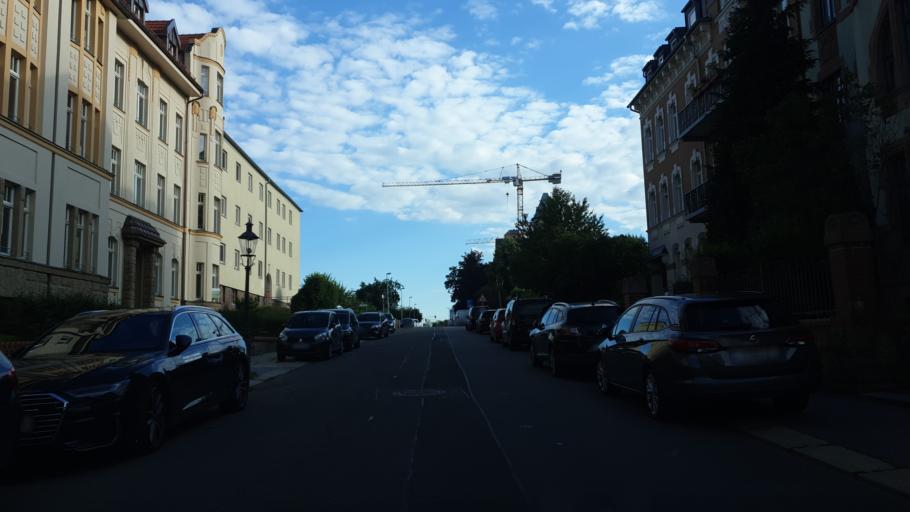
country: DE
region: Saxony
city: Chemnitz
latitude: 50.8376
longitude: 12.9477
